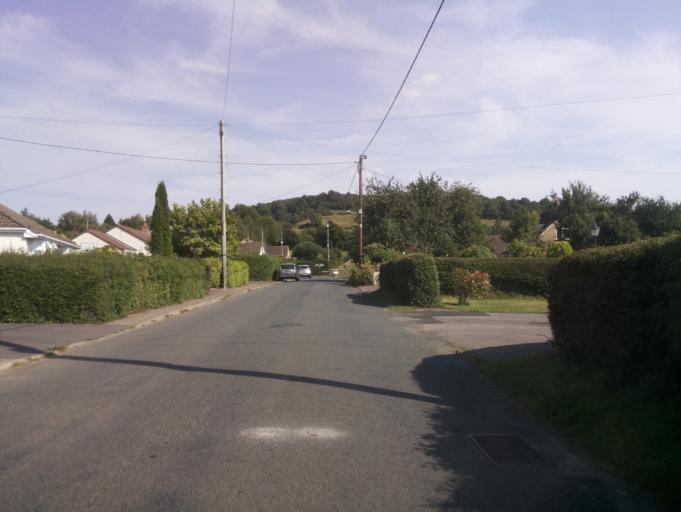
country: GB
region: England
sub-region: Gloucestershire
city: Dursley
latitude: 51.6978
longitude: -2.3398
